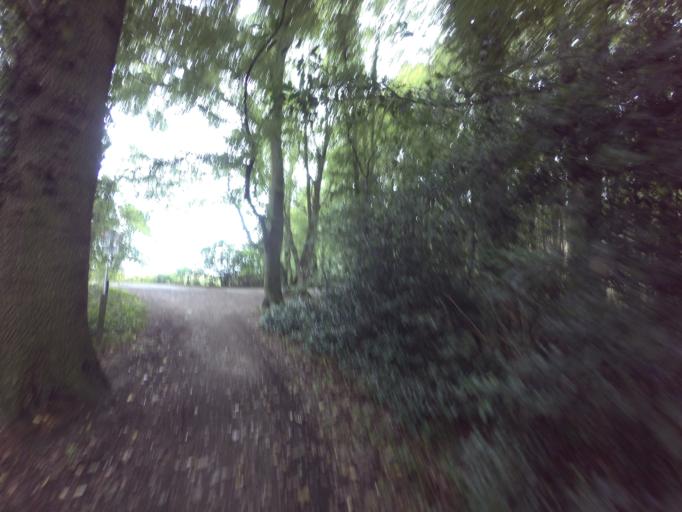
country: NL
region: Limburg
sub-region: Valkenburg aan de Geul
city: Schin op Geul
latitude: 50.7856
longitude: 5.8873
